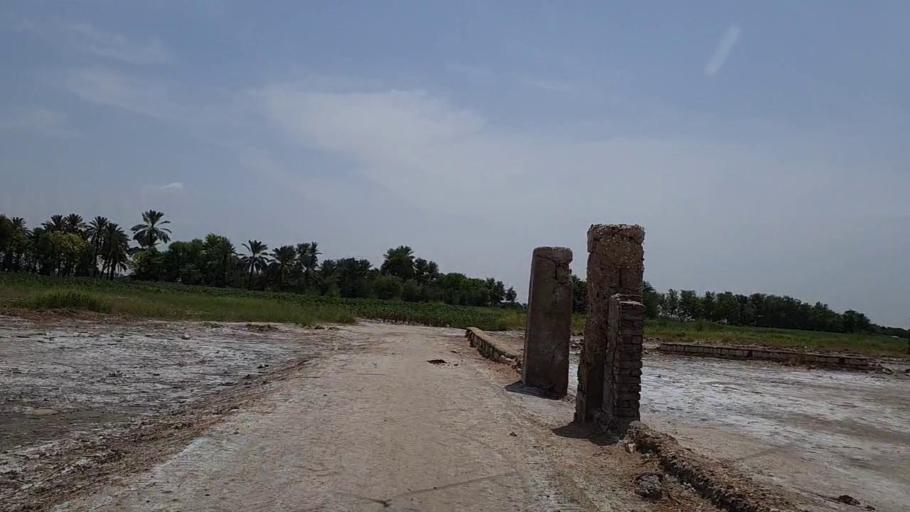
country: PK
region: Sindh
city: Khanpur
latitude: 27.7907
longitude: 69.4567
